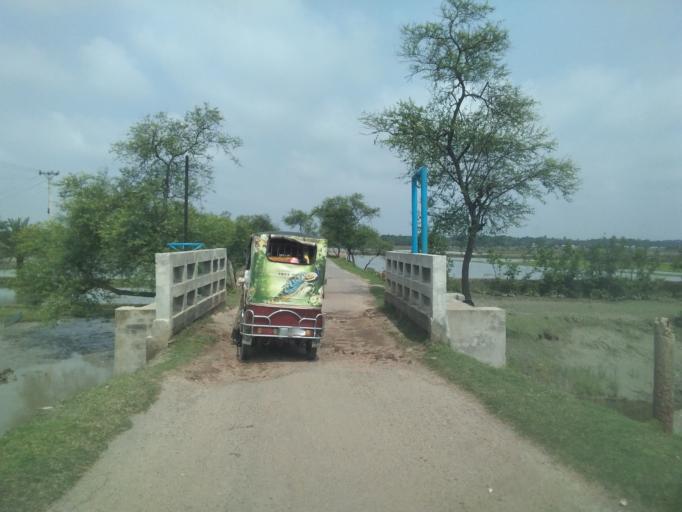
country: BD
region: Khulna
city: Phultala
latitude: 22.7052
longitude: 89.4625
